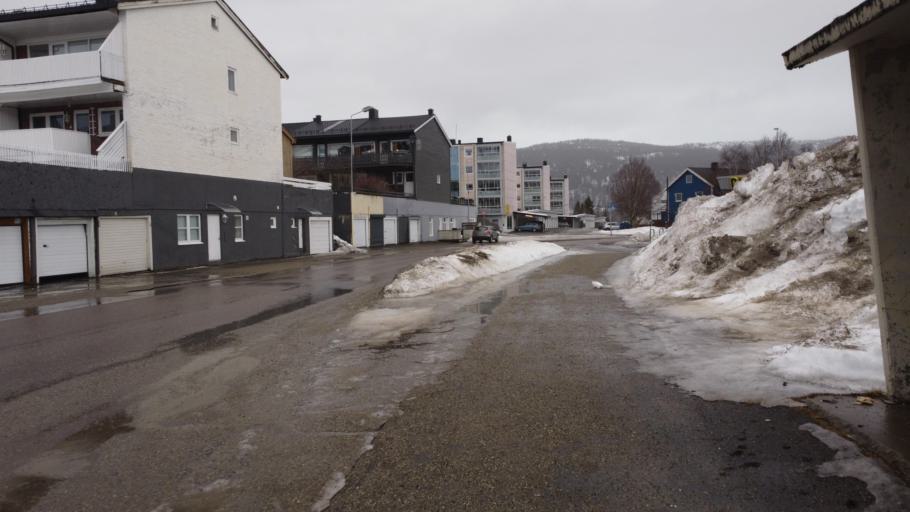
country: NO
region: Nordland
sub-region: Rana
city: Mo i Rana
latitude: 66.3173
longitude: 14.1582
